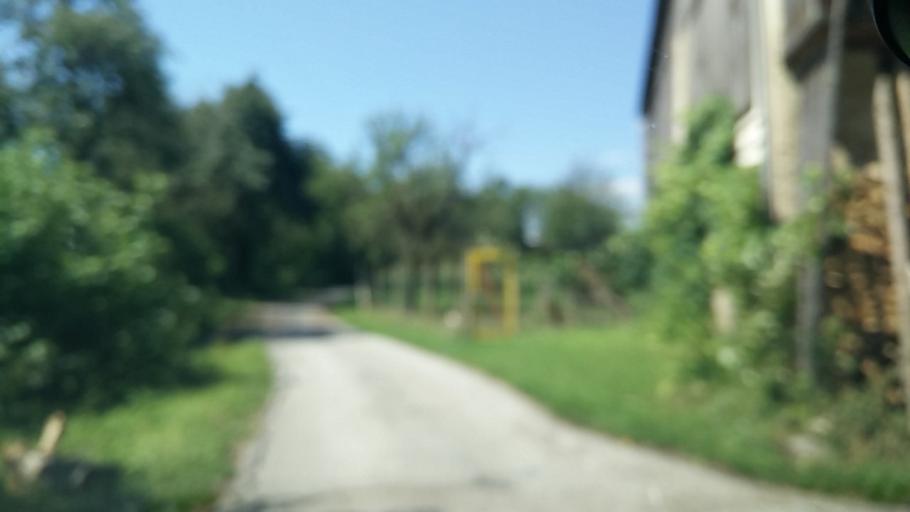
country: AT
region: Carinthia
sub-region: Politischer Bezirk Volkermarkt
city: Sittersdorf
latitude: 46.5438
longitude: 14.5900
